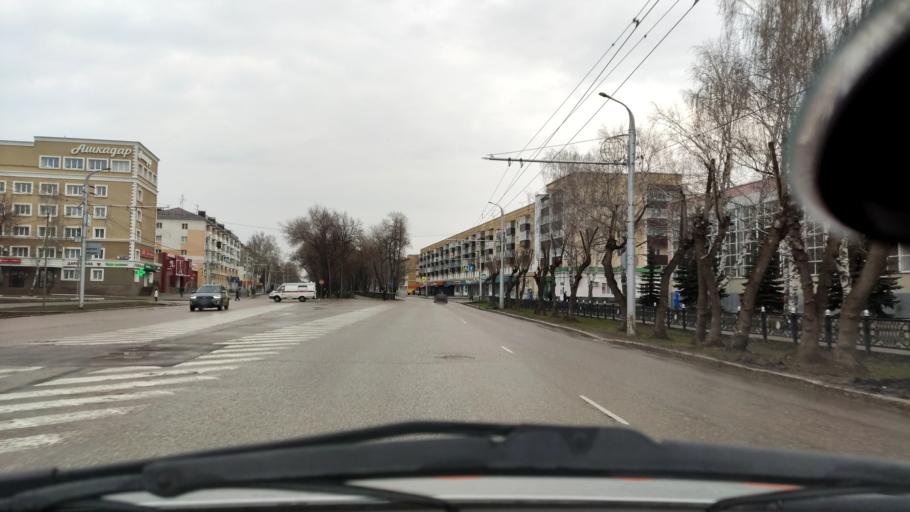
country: RU
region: Bashkortostan
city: Sterlitamak
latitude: 53.6377
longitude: 55.9371
